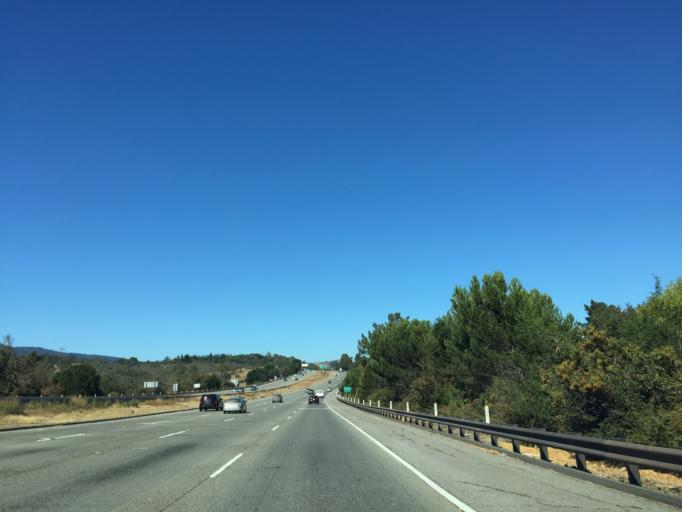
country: US
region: California
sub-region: San Mateo County
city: Woodside
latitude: 37.4240
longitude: -122.2280
